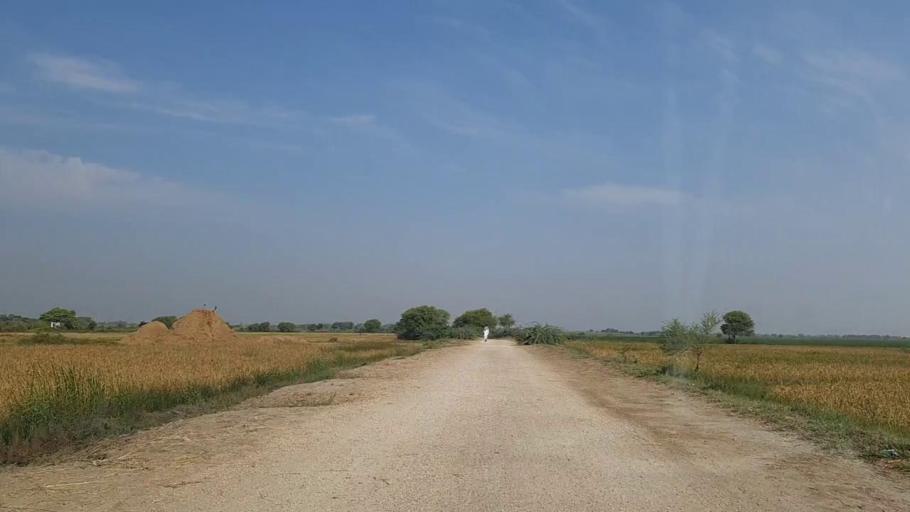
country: PK
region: Sindh
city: Mirpur Batoro
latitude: 24.7084
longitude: 68.2232
